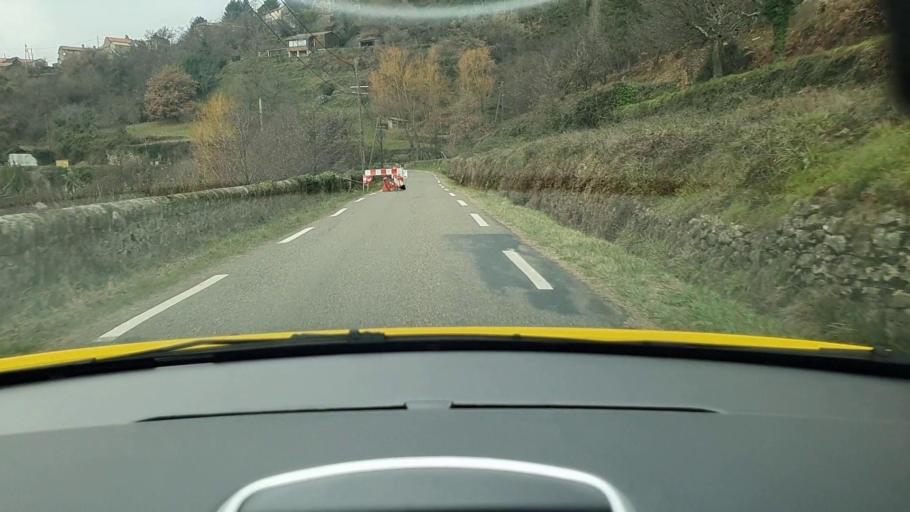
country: FR
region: Languedoc-Roussillon
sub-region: Departement du Gard
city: Besseges
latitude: 44.3396
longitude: 4.0466
